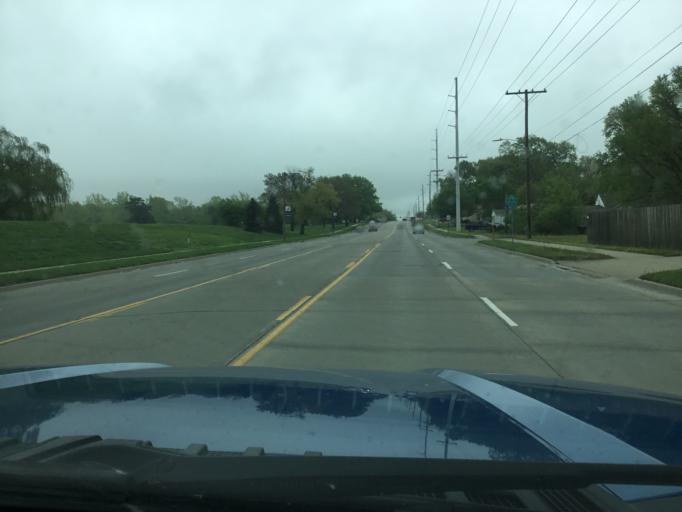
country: US
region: Kansas
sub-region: Shawnee County
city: Topeka
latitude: 39.0296
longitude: -95.7015
